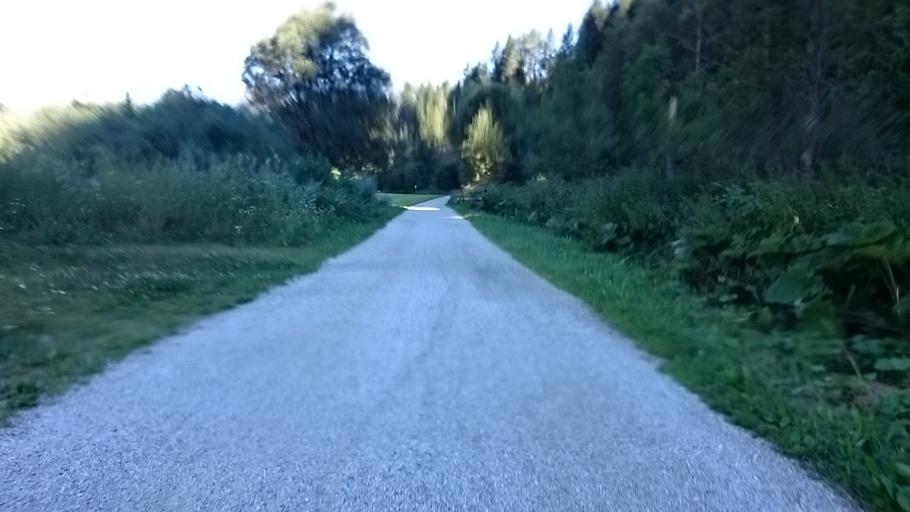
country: IT
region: Trentino-Alto Adige
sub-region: Bolzano
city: Monguelfo
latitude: 46.7576
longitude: 12.0988
